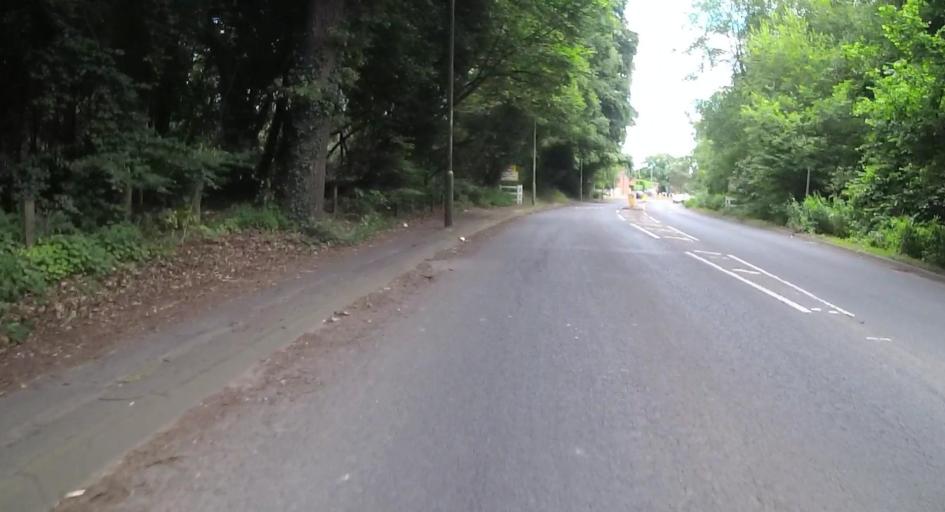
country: GB
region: England
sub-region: Hampshire
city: Fleet
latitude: 51.2562
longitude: -0.8259
